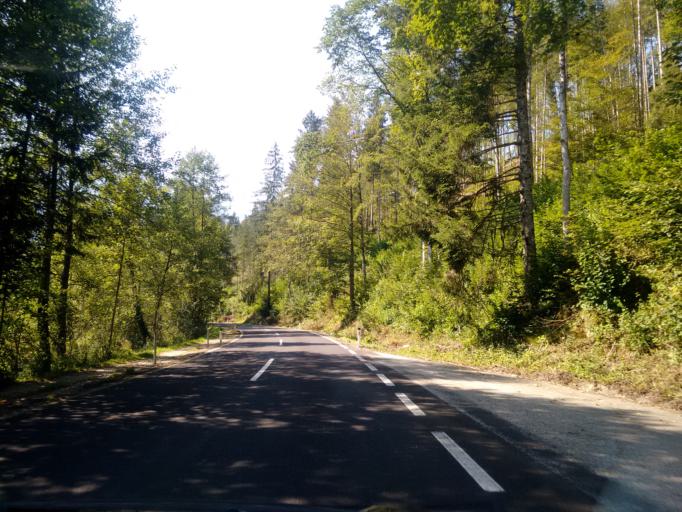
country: AT
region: Upper Austria
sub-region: Politischer Bezirk Gmunden
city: Gruenau im Almtal
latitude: 47.7565
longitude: 13.9525
